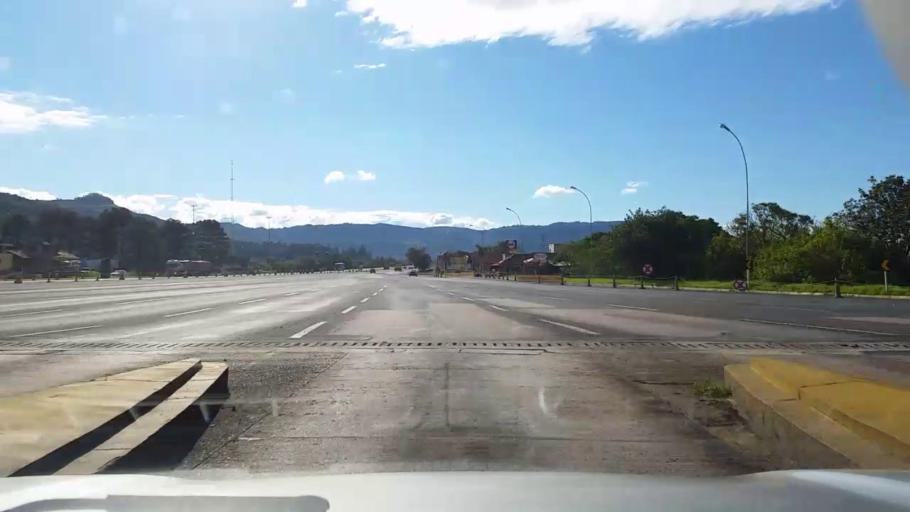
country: BR
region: Rio Grande do Sul
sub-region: Osorio
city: Osorio
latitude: -29.8854
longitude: -50.4471
